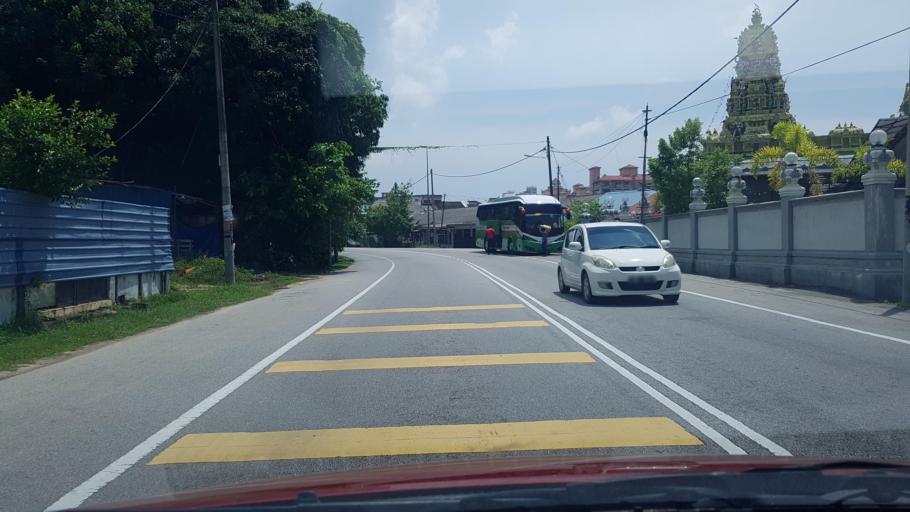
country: MY
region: Terengganu
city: Kuala Terengganu
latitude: 5.3223
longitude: 103.1390
